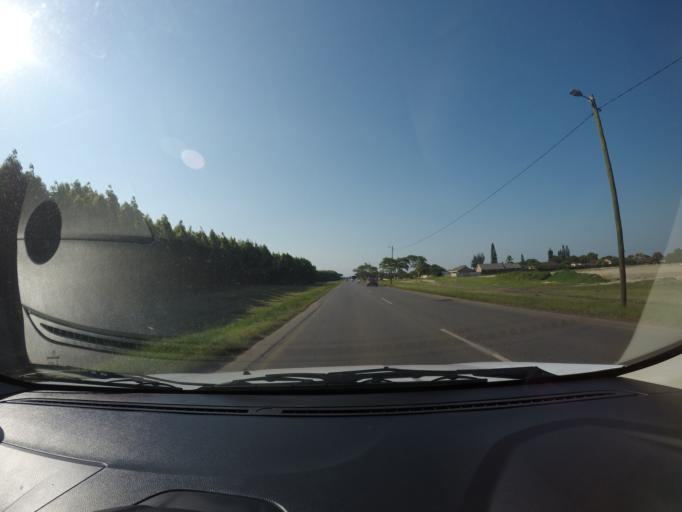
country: ZA
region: KwaZulu-Natal
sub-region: uThungulu District Municipality
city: Richards Bay
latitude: -28.7200
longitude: 32.0331
